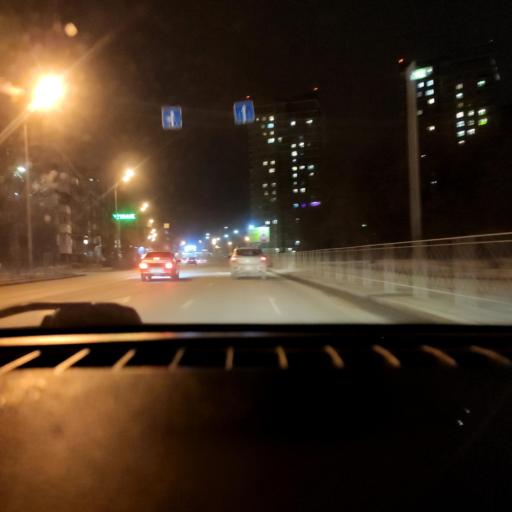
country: RU
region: Perm
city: Perm
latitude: 57.9933
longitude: 56.1923
